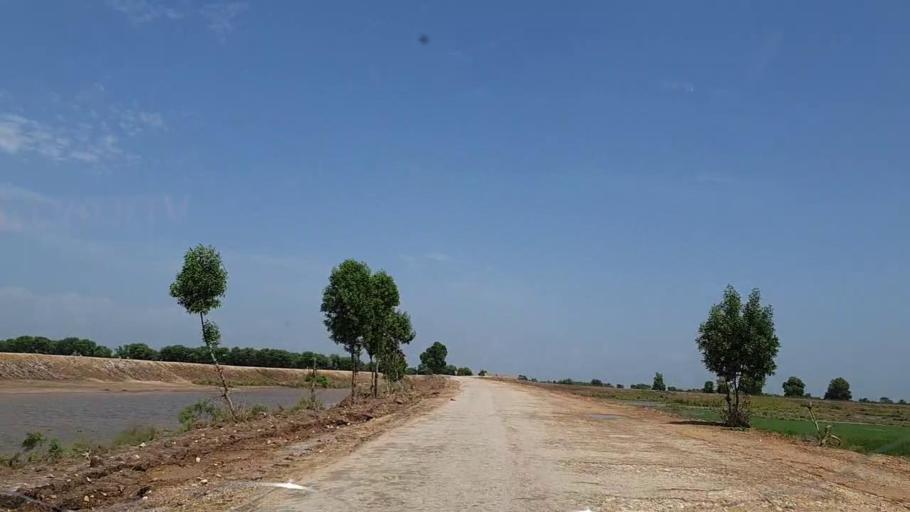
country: PK
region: Sindh
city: Naushahro Firoz
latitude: 26.8253
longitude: 68.1551
